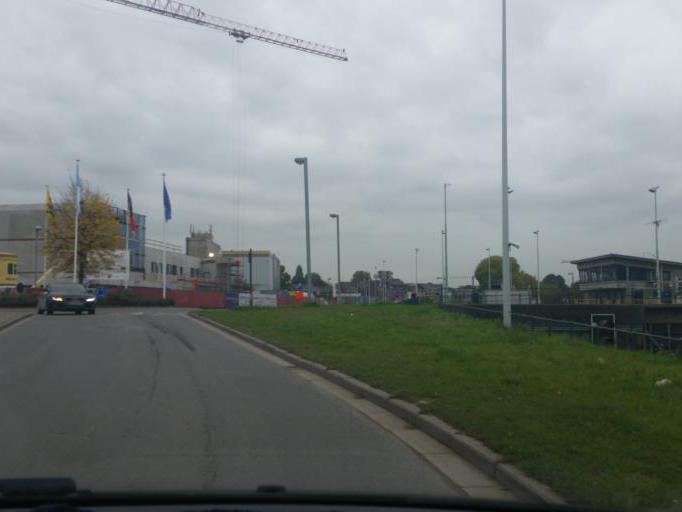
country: BE
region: Flanders
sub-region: Provincie Vlaams-Brabant
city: Halle
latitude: 50.7393
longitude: 4.2418
